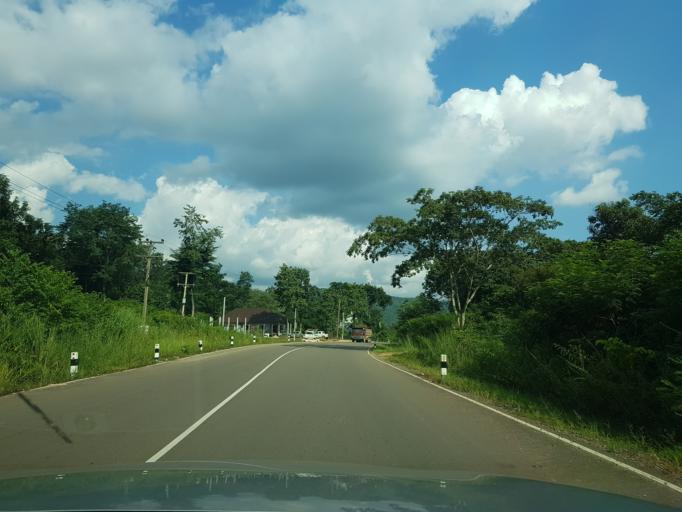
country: TH
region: Nong Khai
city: Sangkhom
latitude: 18.0317
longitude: 102.3710
